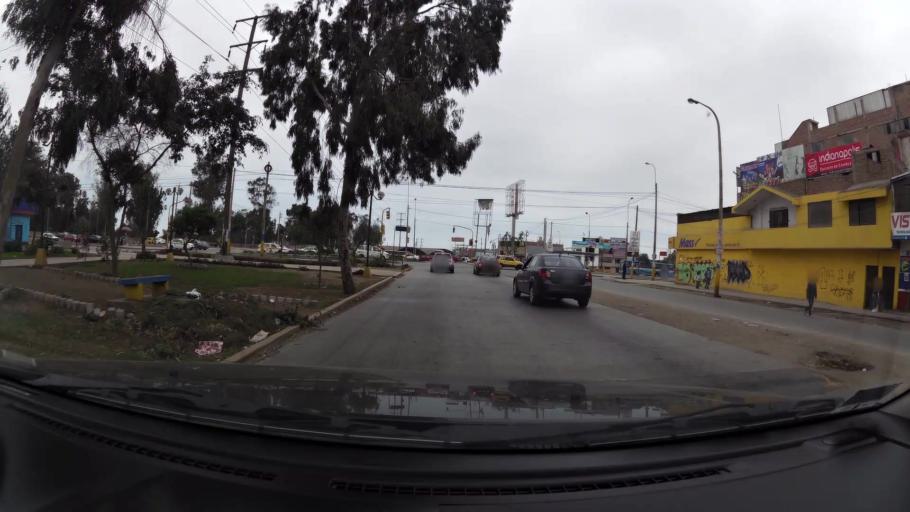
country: PE
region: Lima
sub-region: Lima
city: Surco
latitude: -12.1977
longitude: -76.9571
